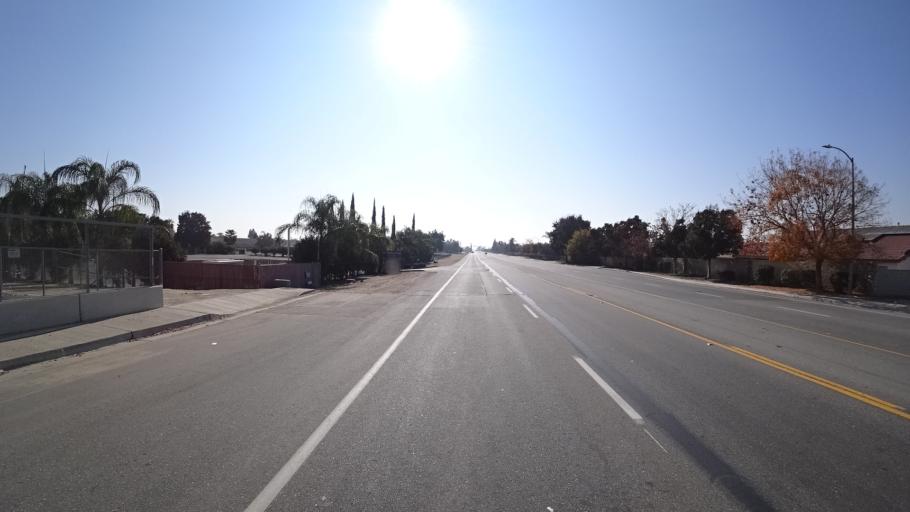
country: US
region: California
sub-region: Kern County
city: Greenfield
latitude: 35.2920
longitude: -119.0389
